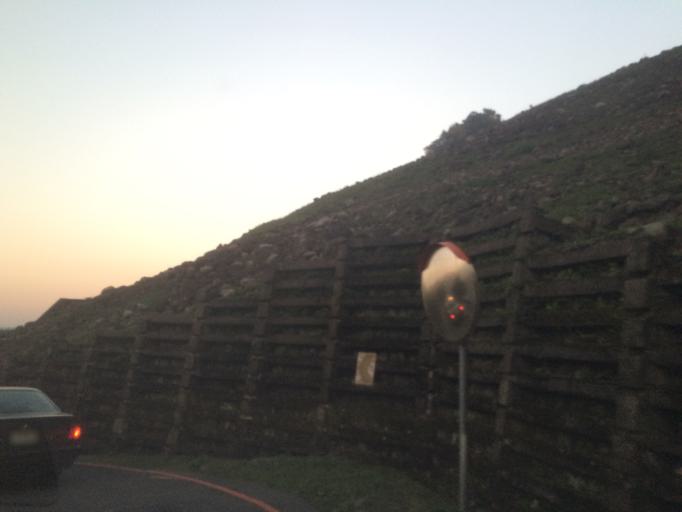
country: TW
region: Taiwan
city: Daxi
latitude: 24.8120
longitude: 121.2446
